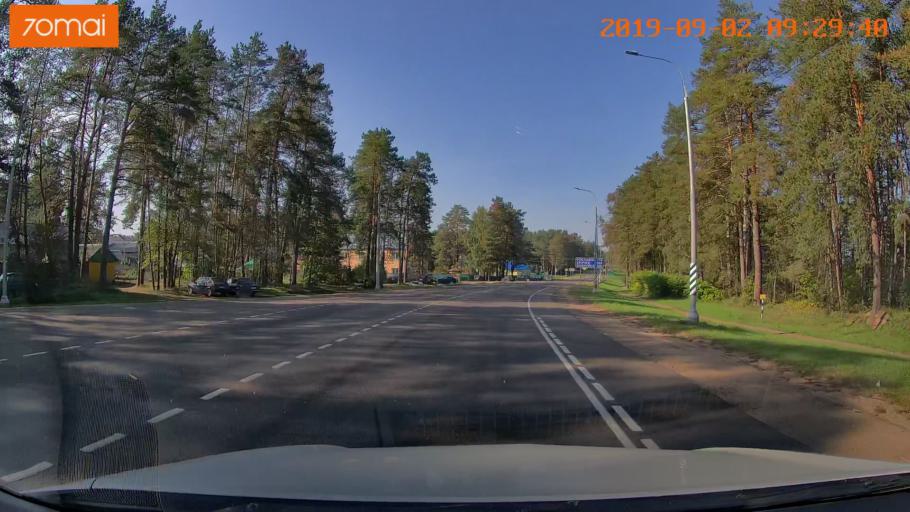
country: RU
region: Kaluga
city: Yukhnov
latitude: 54.7388
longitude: 35.2122
